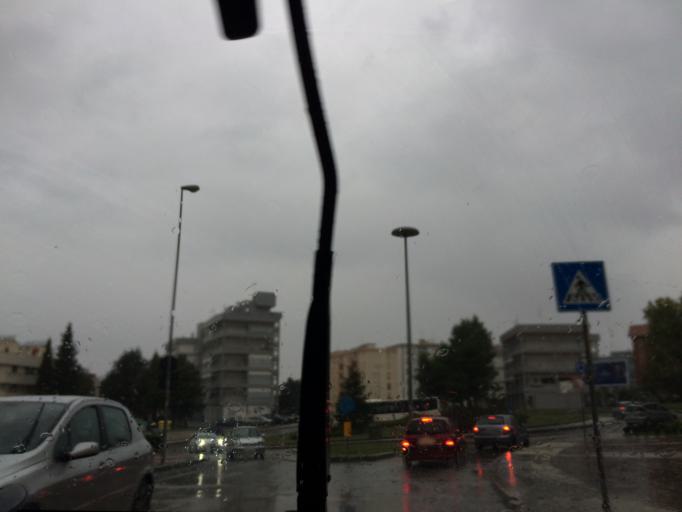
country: IT
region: Basilicate
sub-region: Provincia di Matera
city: Matera
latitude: 40.6730
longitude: 16.5868
